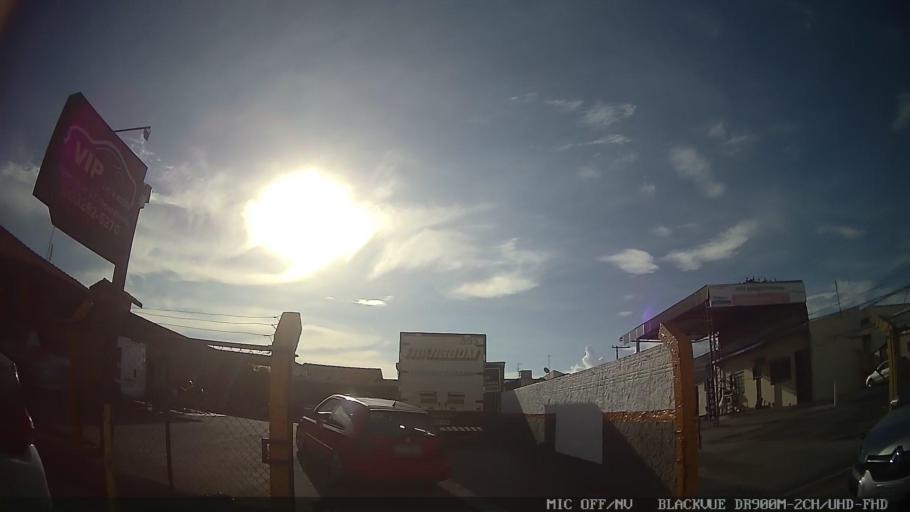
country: BR
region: Sao Paulo
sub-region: Tiete
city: Tiete
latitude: -23.1132
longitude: -47.7110
